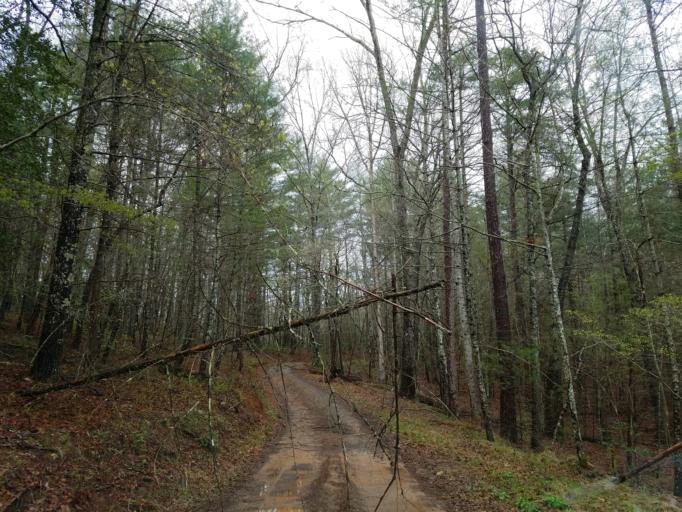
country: US
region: Georgia
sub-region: Fannin County
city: Blue Ridge
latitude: 34.7987
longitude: -84.2428
